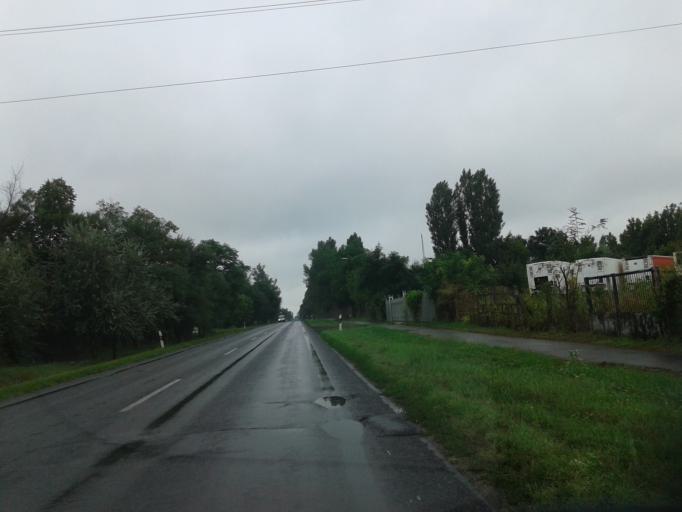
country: HU
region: Bacs-Kiskun
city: Kiskoros
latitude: 46.6097
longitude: 19.3014
